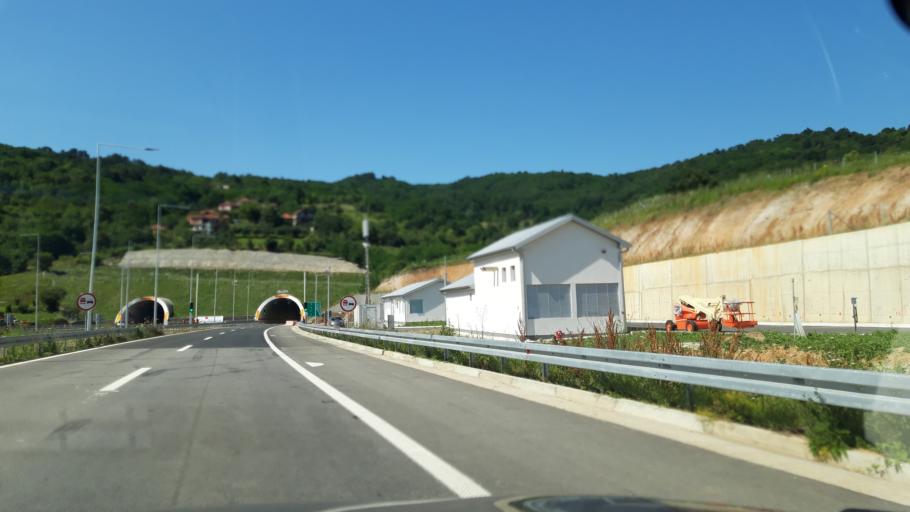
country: RS
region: Central Serbia
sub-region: Pcinjski Okrug
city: Vladicin Han
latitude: 42.7291
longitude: 22.0736
